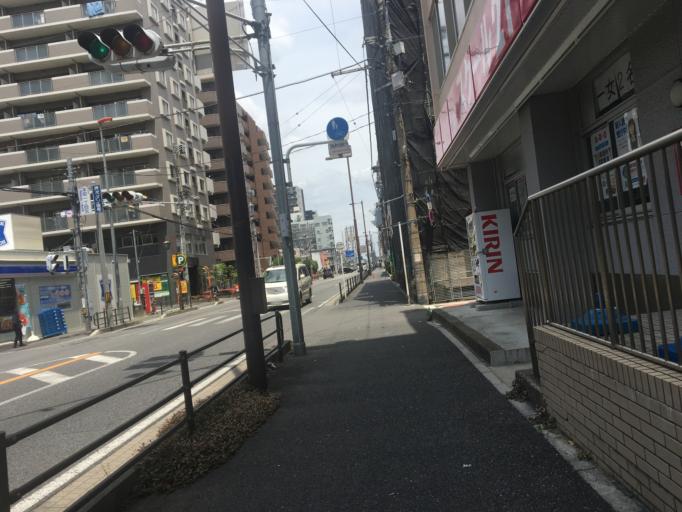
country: JP
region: Saitama
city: Shimotoda
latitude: 35.8100
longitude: 139.6828
